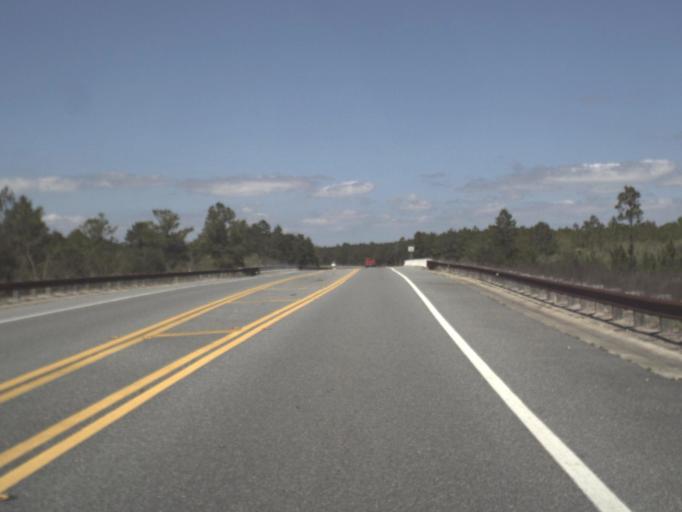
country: US
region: Florida
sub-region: Gulf County
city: Port Saint Joe
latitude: 29.8708
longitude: -85.3391
